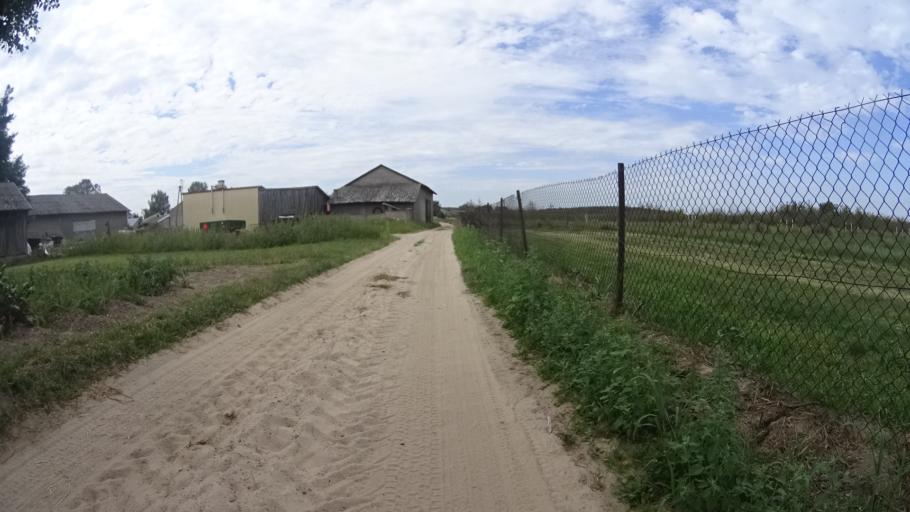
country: PL
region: Masovian Voivodeship
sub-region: Powiat bialobrzeski
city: Wysmierzyce
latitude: 51.6531
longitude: 20.8062
